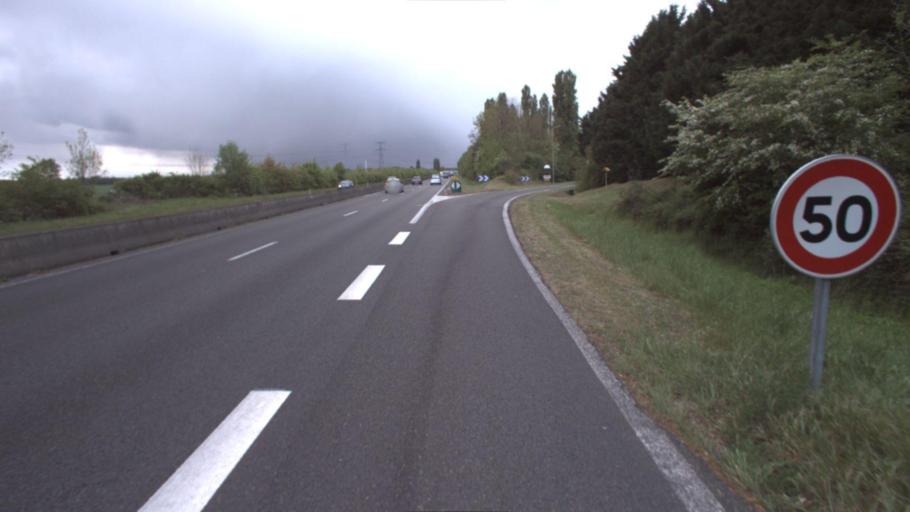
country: FR
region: Ile-de-France
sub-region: Departement de Seine-et-Marne
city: Ozoir-la-Ferriere
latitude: 48.7561
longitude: 2.6730
